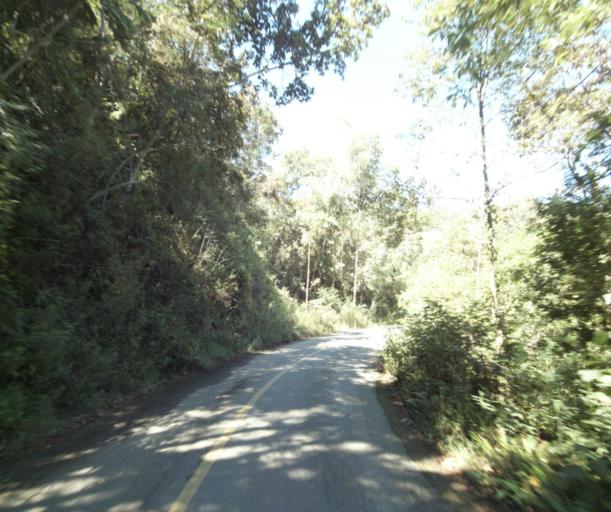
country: BR
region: Minas Gerais
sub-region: Espera Feliz
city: Espera Feliz
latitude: -20.6245
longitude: -41.8156
